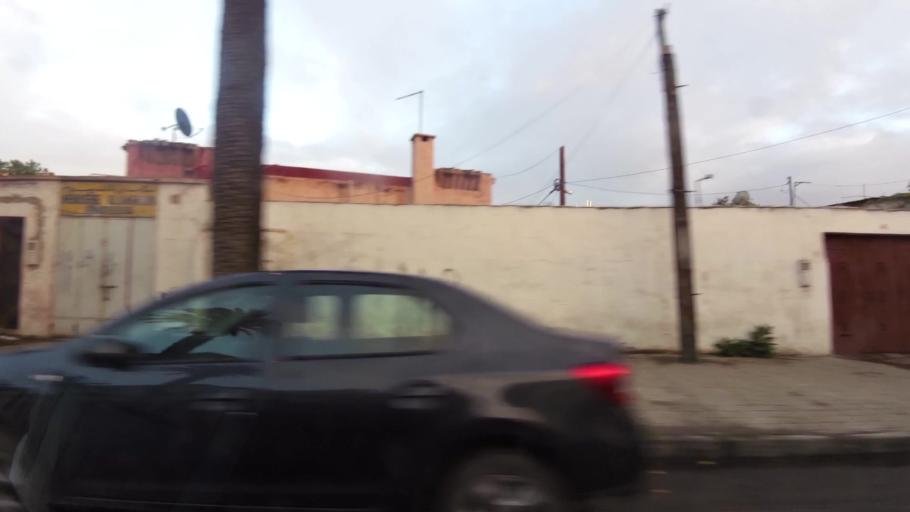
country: MA
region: Grand Casablanca
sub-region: Casablanca
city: Casablanca
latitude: 33.5766
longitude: -7.6396
